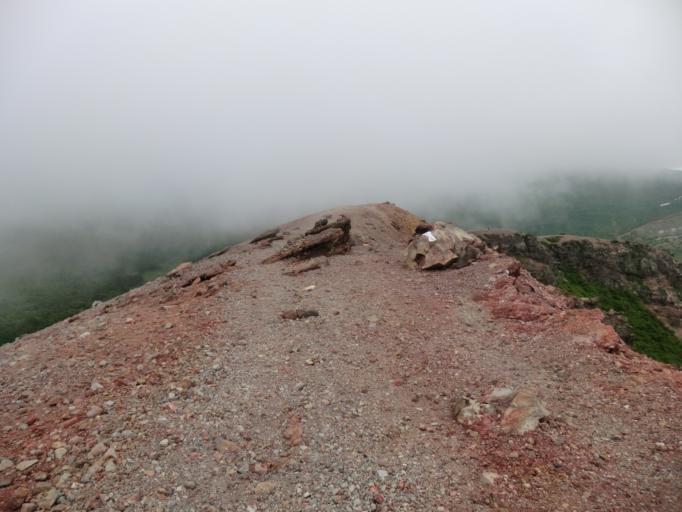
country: JP
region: Fukushima
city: Fukushima-shi
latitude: 37.7202
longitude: 140.2624
